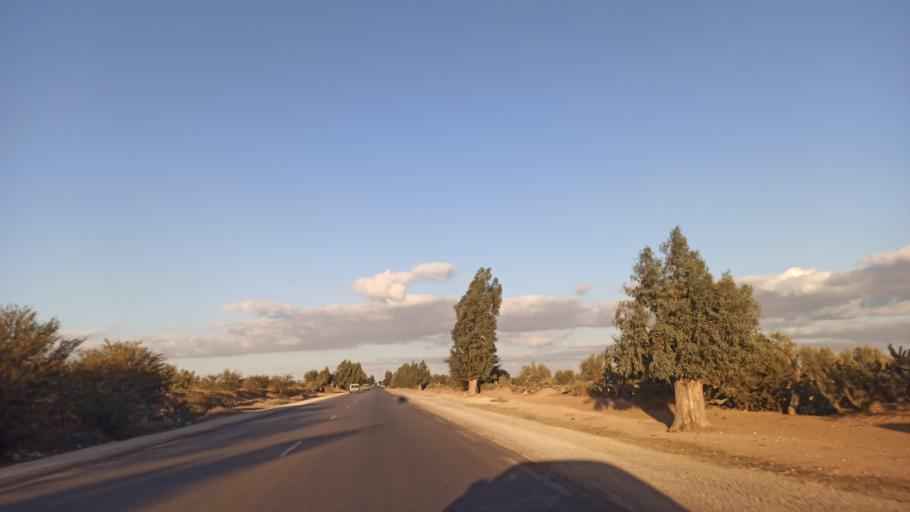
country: TN
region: Al Qayrawan
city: Sbikha
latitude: 35.8664
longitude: 10.2122
